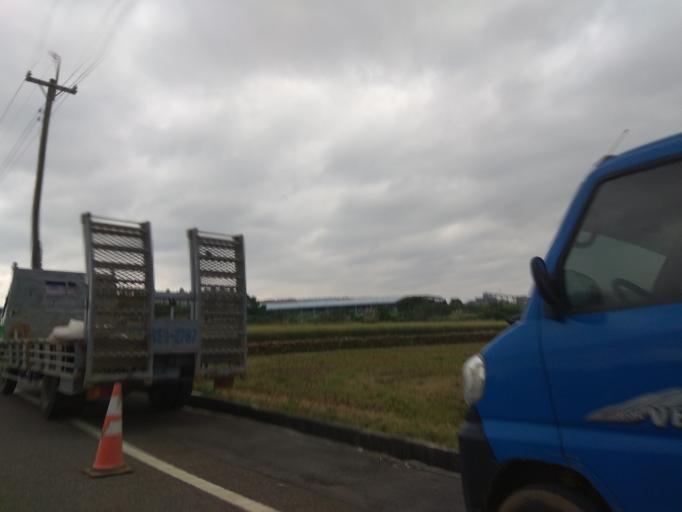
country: TW
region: Taiwan
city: Taoyuan City
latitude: 25.0281
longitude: 121.2219
